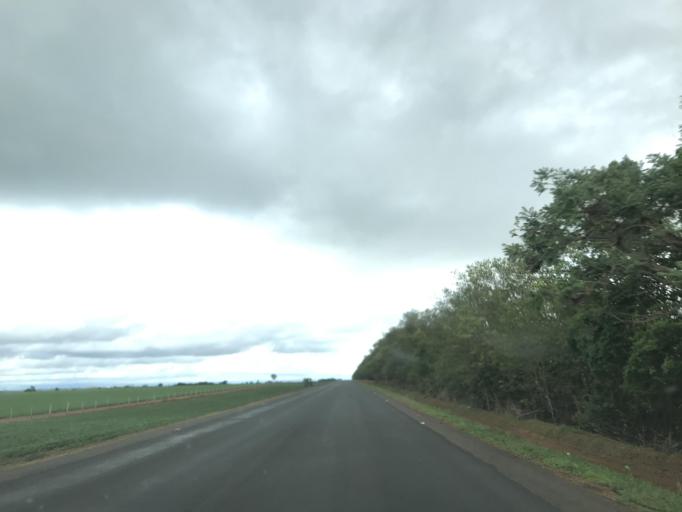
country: BR
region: Goias
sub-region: Vianopolis
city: Vianopolis
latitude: -16.7979
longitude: -48.5201
